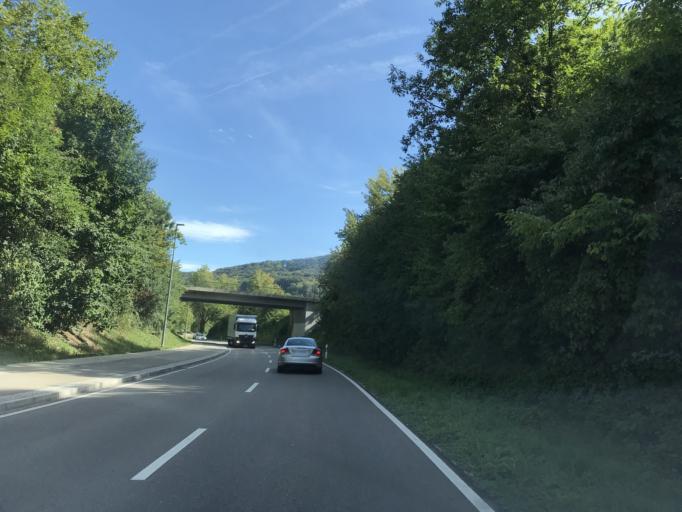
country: DE
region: Baden-Wuerttemberg
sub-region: Freiburg Region
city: Bad Sackingen
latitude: 47.5508
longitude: 7.9365
